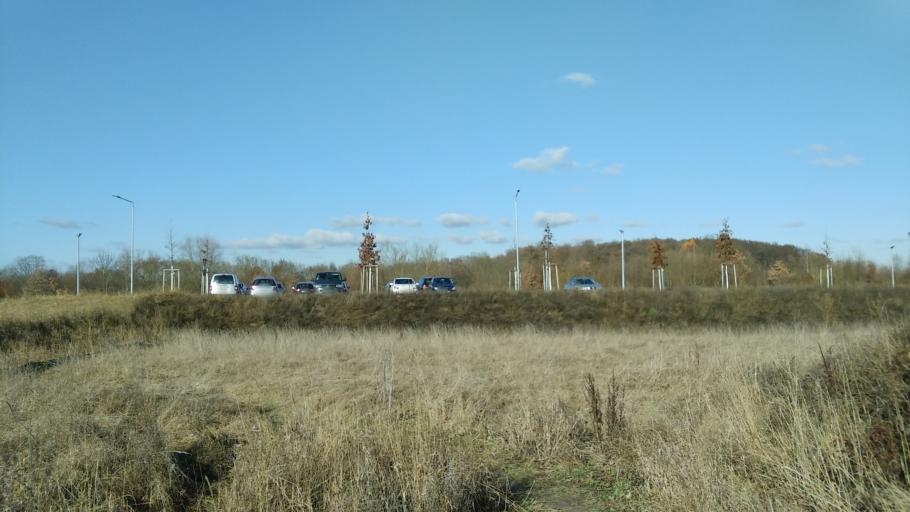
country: DE
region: Baden-Wuerttemberg
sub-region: Tuebingen Region
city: Wannweil
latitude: 48.4965
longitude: 9.1401
